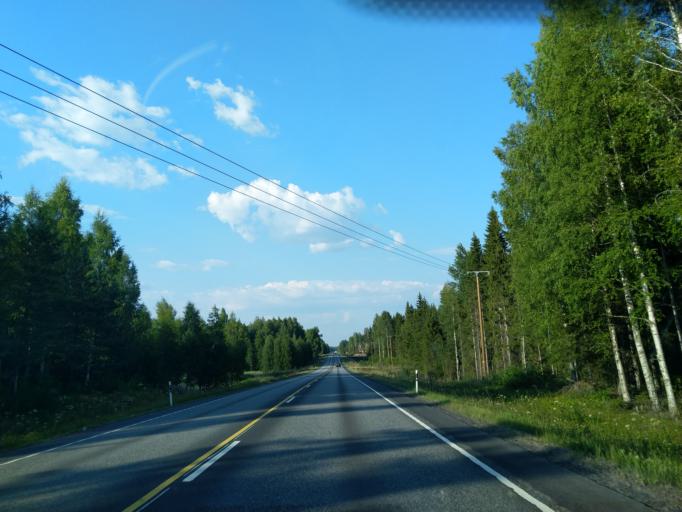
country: FI
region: Satakunta
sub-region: Pori
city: Pomarkku
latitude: 61.7253
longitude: 22.0620
